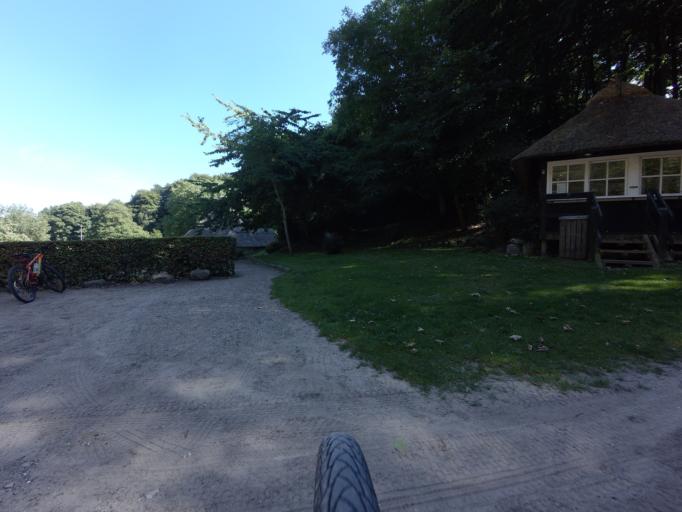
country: DK
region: Zealand
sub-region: Vordingborg Kommune
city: Stege
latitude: 54.9994
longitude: 12.5226
